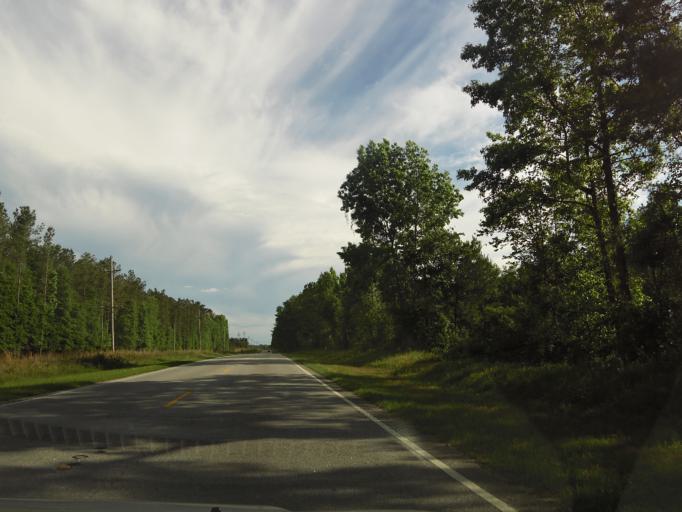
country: US
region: South Carolina
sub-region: Allendale County
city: Fairfax
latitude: 32.8895
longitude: -81.2381
